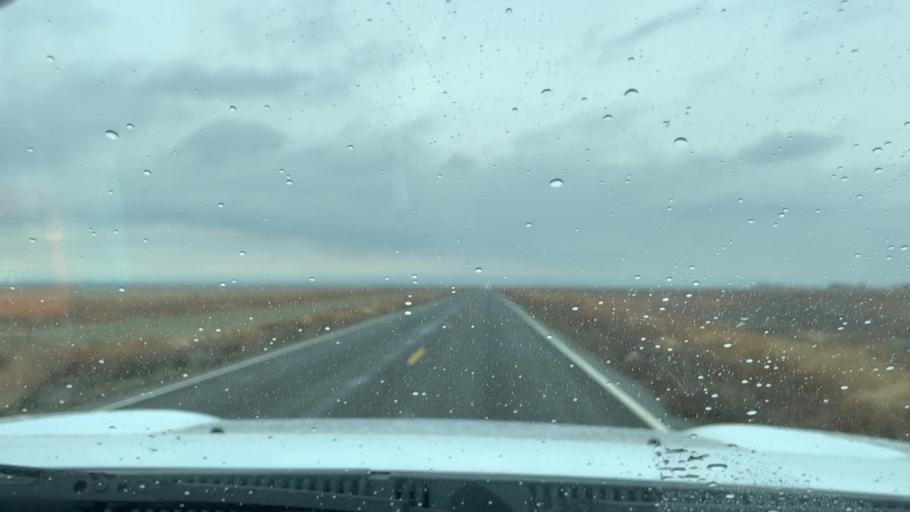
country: US
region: California
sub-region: Kings County
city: Kettleman City
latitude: 35.9340
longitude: -119.7980
